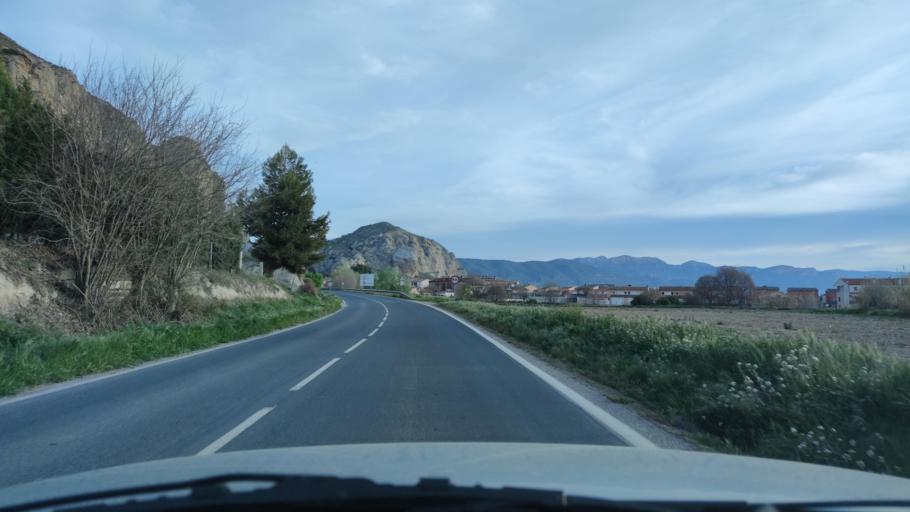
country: ES
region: Catalonia
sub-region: Provincia de Lleida
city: Balaguer
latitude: 41.8175
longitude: 0.8041
